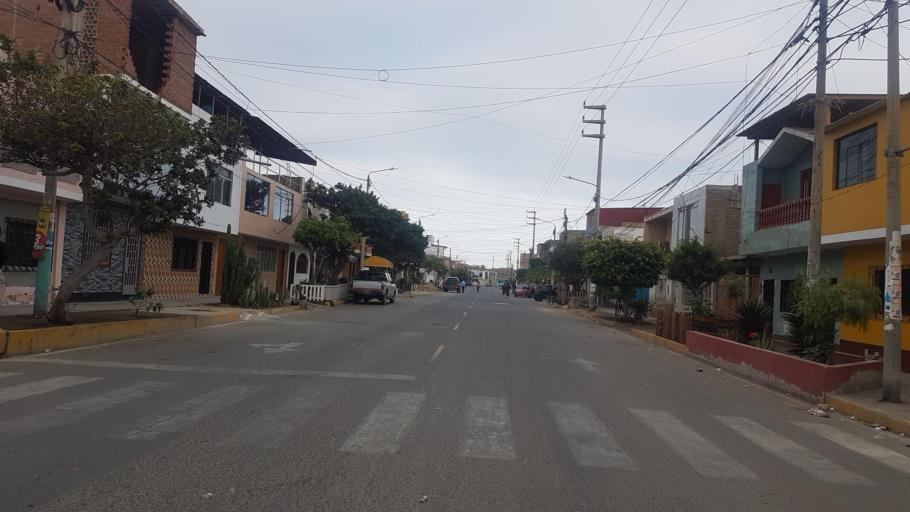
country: PE
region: Ancash
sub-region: Provincia de Santa
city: Chimbote
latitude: -9.0933
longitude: -78.5714
